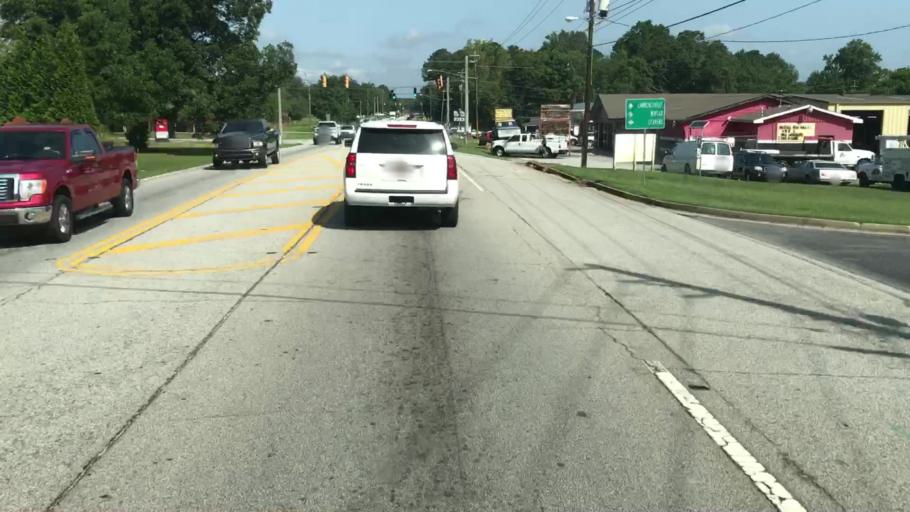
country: US
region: Georgia
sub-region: Walton County
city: Loganville
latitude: 33.8407
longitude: -83.8952
